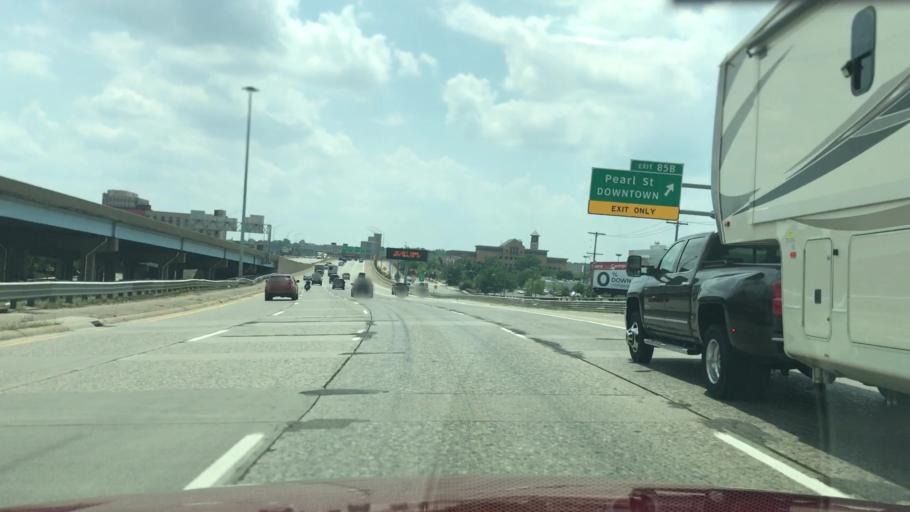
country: US
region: Michigan
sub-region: Kent County
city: Grand Rapids
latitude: 42.9700
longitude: -85.6787
